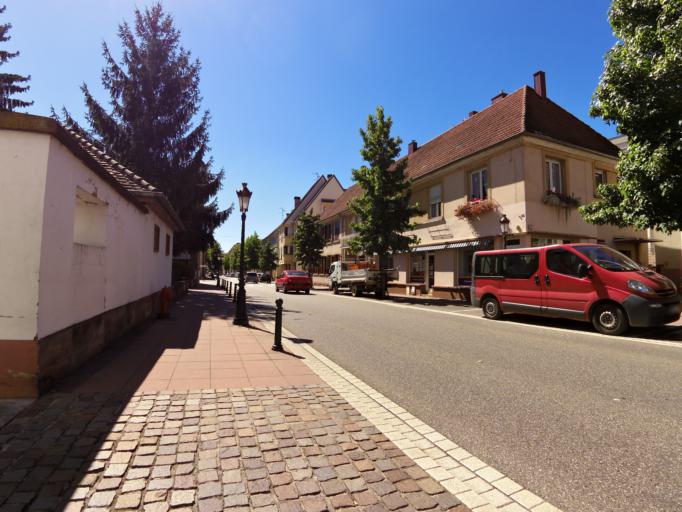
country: FR
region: Alsace
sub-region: Departement du Bas-Rhin
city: Haguenau
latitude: 48.8201
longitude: 7.7914
